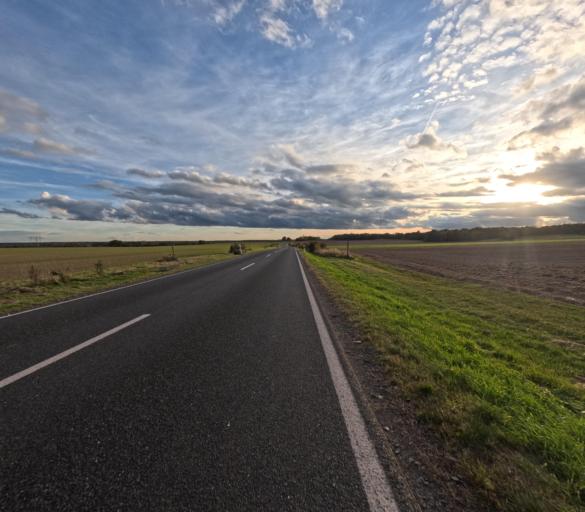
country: DE
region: Saxony
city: Grimma
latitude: 51.2550
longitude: 12.6804
